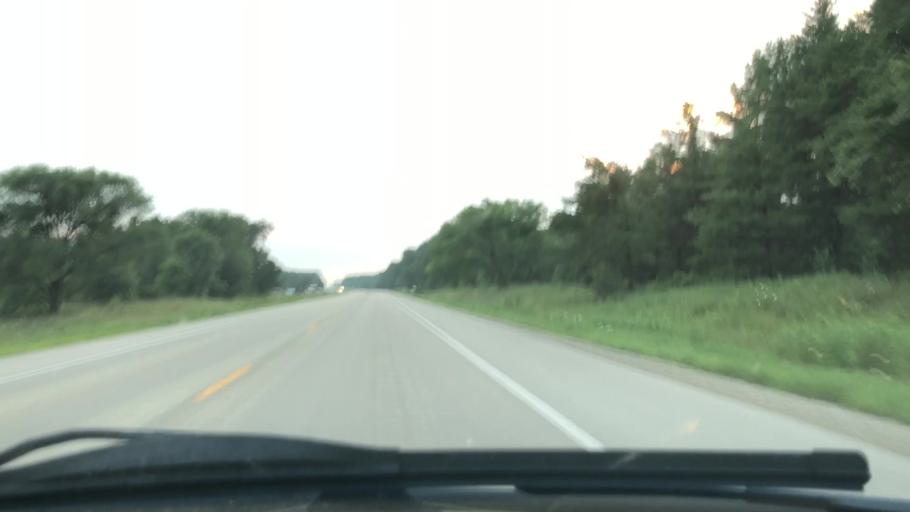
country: US
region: Wisconsin
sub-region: Sauk County
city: Spring Green
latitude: 43.1906
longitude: -90.1535
